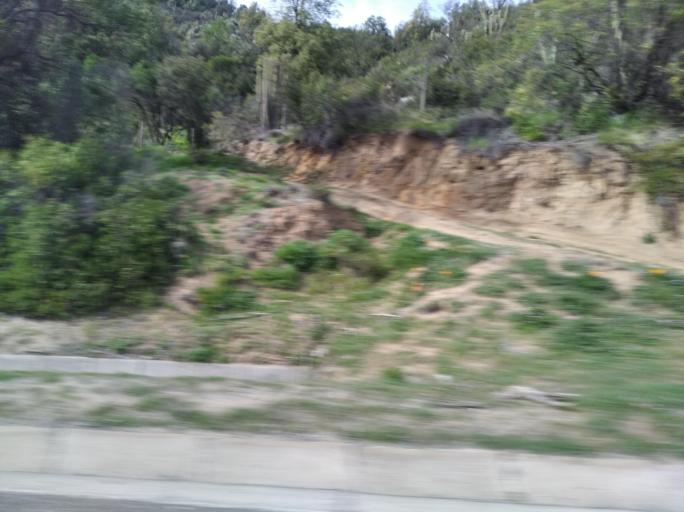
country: CL
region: Valparaiso
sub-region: Provincia de San Felipe
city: Llaillay
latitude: -33.0632
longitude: -71.0162
